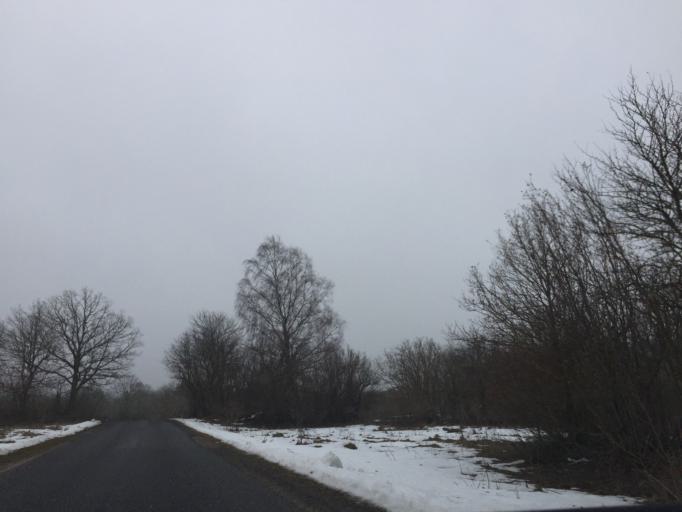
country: EE
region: Saare
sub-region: Kuressaare linn
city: Kuressaare
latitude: 58.2730
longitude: 22.5763
